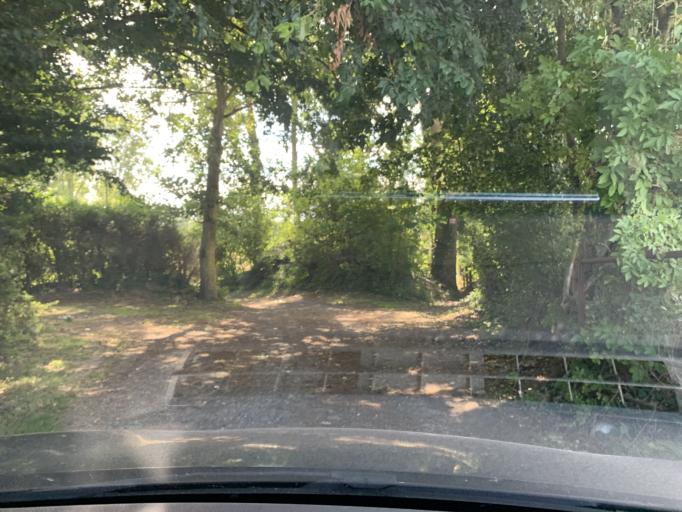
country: FR
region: Nord-Pas-de-Calais
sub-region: Departement du Nord
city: Fontaine-Notre-Dame
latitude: 50.1500
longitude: 3.1746
